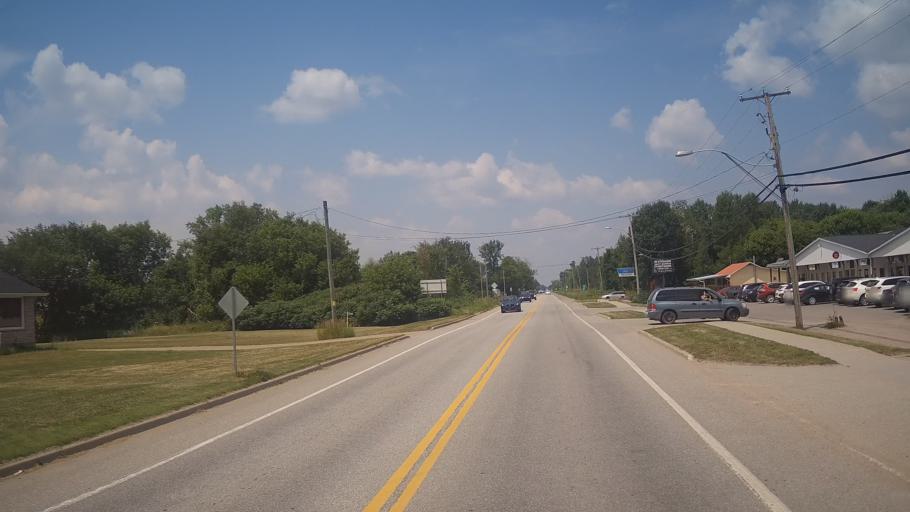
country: CA
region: Quebec
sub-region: Outaouais
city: Shawville
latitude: 45.6000
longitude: -76.4946
